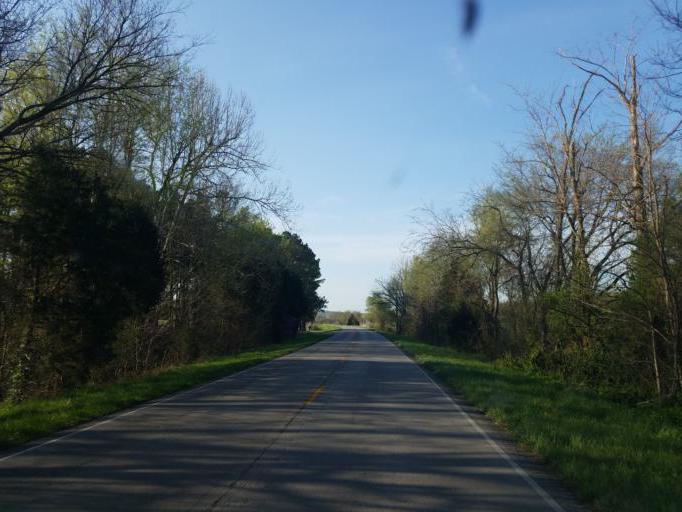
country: US
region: Kentucky
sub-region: Hart County
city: Munfordville
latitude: 37.4367
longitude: -85.8921
